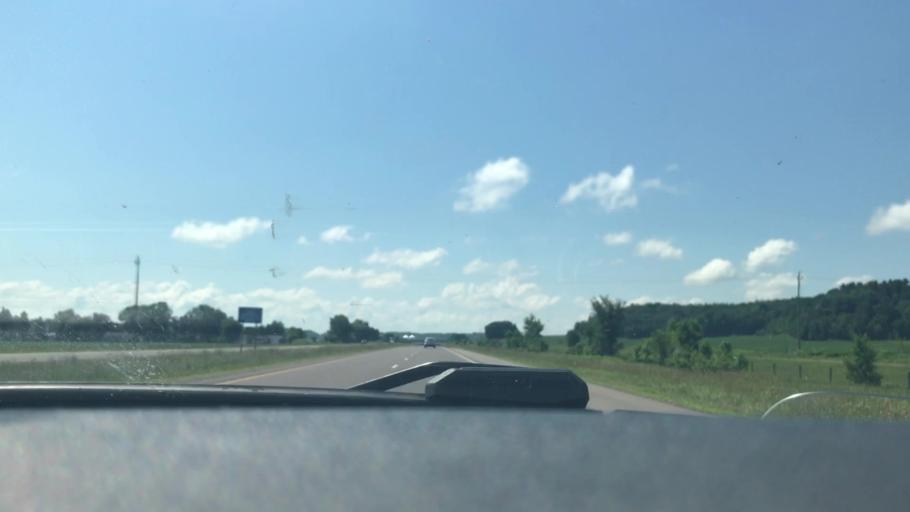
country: US
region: Wisconsin
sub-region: Chippewa County
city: Chippewa Falls
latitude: 45.0106
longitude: -91.4426
